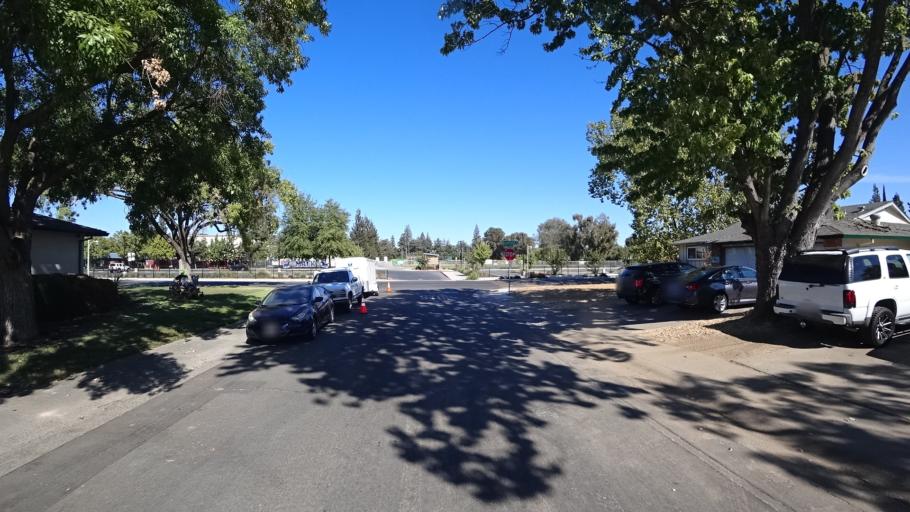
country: US
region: California
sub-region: Sacramento County
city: Parkway
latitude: 38.4795
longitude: -121.4461
